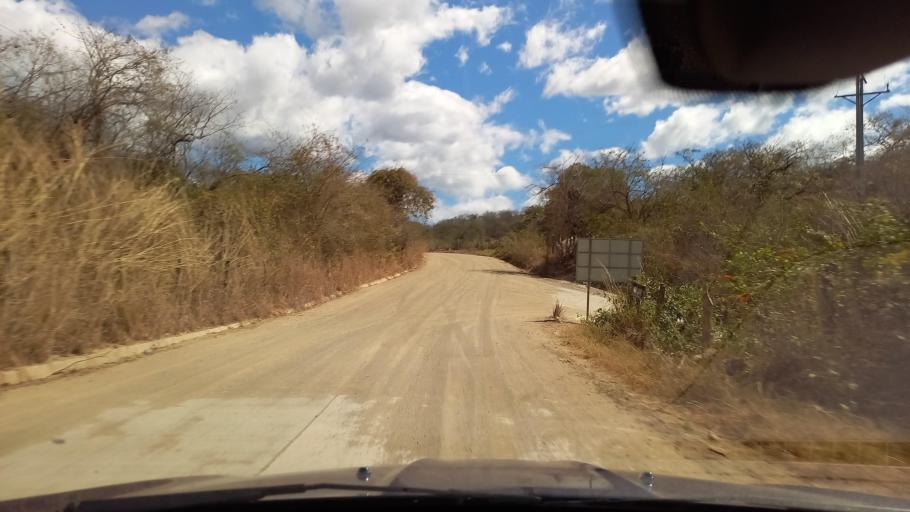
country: SV
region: Santa Ana
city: Metapan
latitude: 14.3593
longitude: -89.4659
